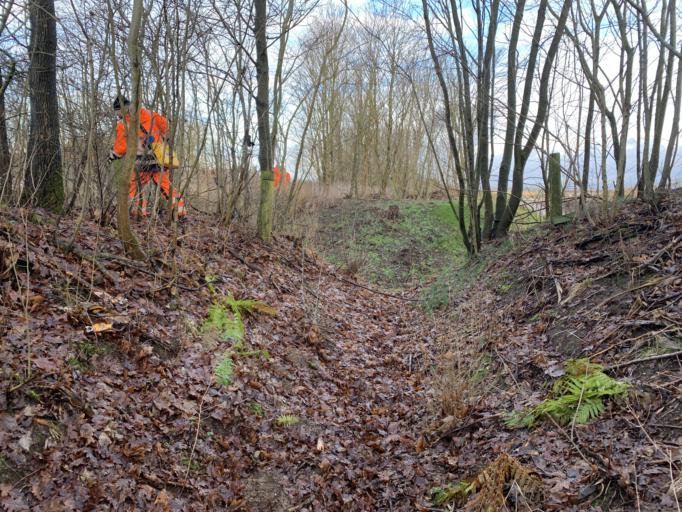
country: DK
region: North Denmark
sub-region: Rebild Kommune
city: Stovring
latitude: 56.8870
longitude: 9.8456
